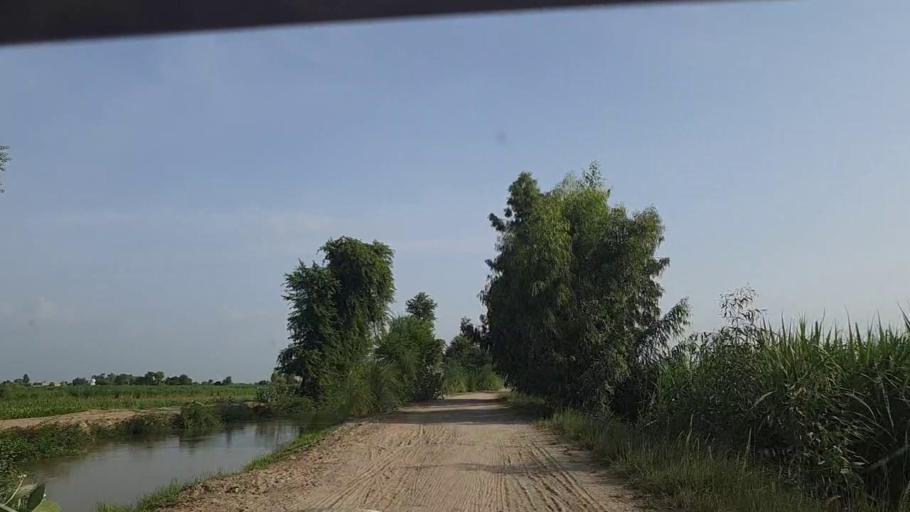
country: PK
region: Sindh
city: Ghotki
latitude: 28.0024
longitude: 69.2618
